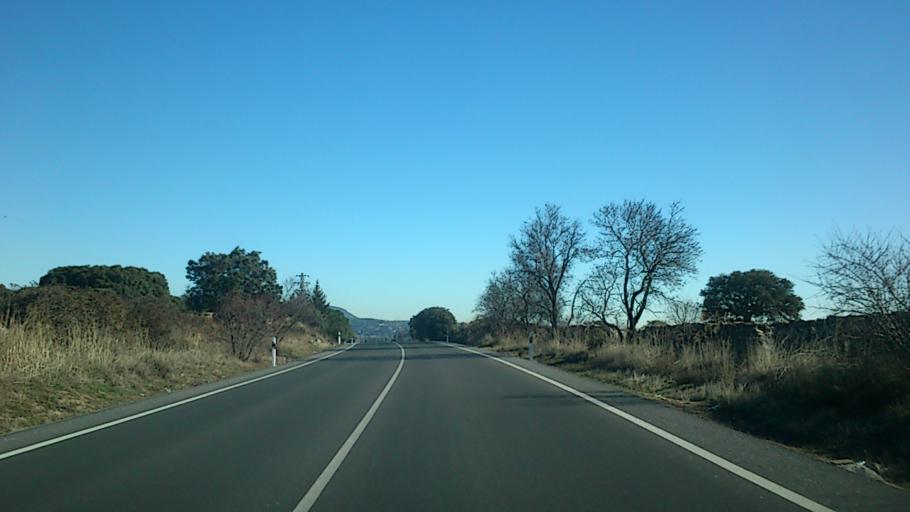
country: ES
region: Madrid
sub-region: Provincia de Madrid
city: Alpedrete
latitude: 40.6504
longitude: -4.0527
